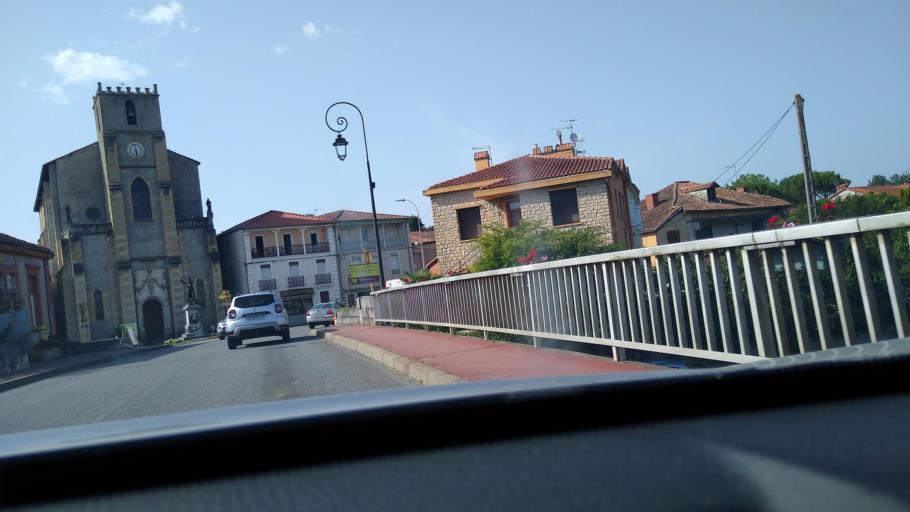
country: FR
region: Midi-Pyrenees
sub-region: Departement de la Haute-Garonne
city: Salies-du-Salat
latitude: 43.0821
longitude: 0.9517
